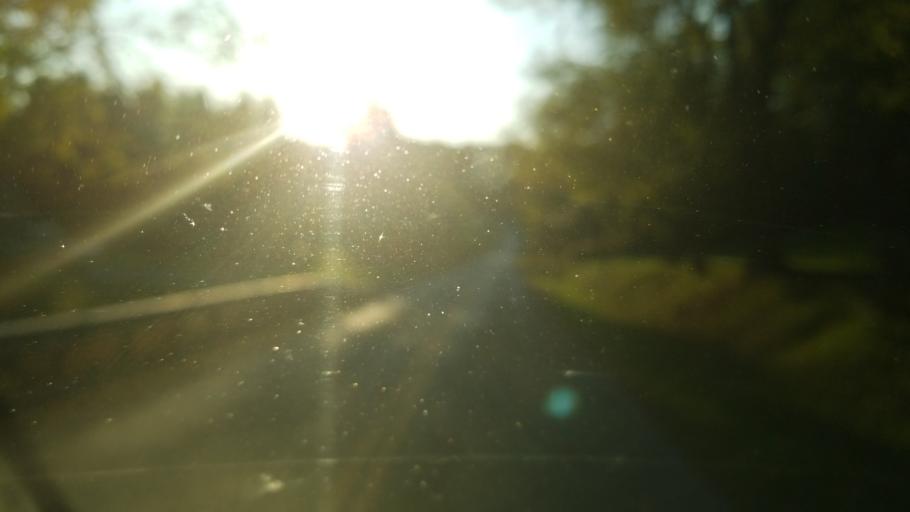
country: US
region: Ohio
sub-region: Sandusky County
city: Bellville
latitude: 40.6242
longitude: -82.4960
